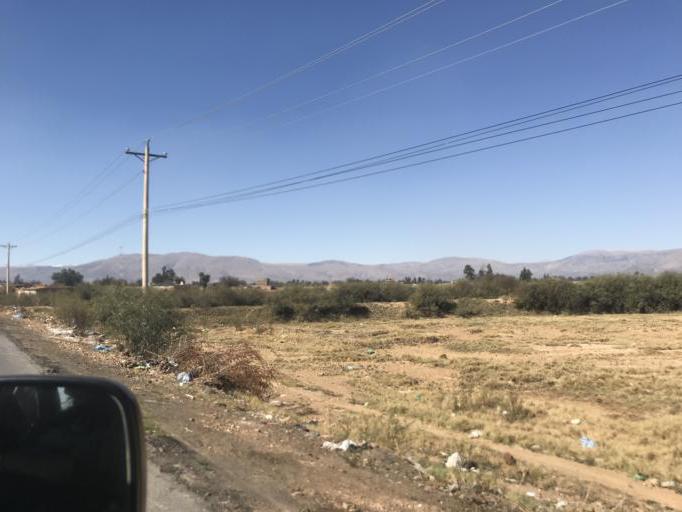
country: BO
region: Cochabamba
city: Cliza
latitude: -17.5689
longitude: -65.8942
